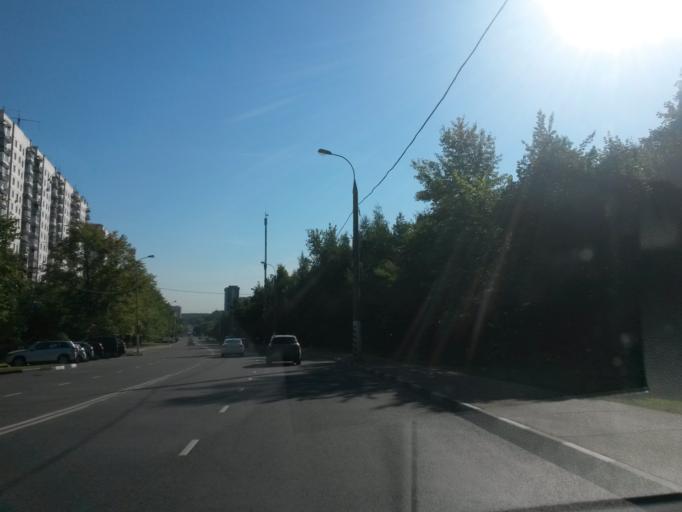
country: RU
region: Moscow
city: Yasenevo
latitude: 55.6118
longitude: 37.5276
